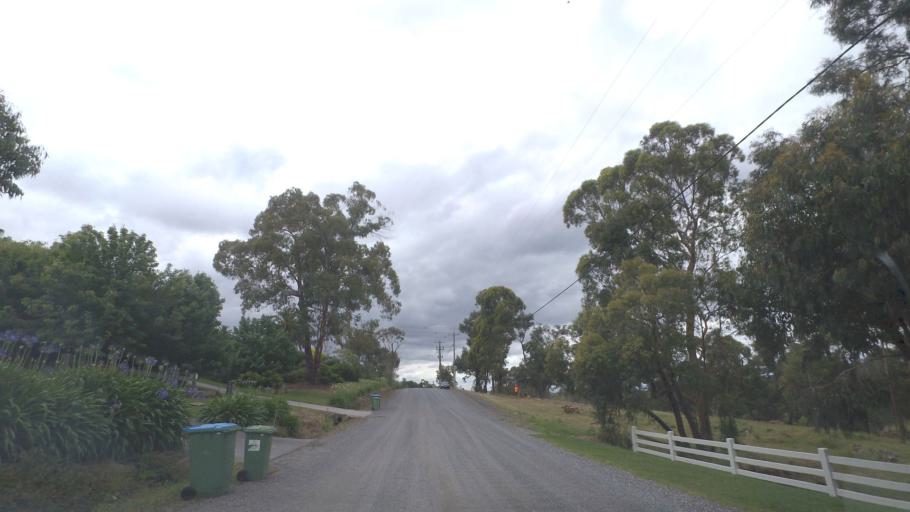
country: AU
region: Victoria
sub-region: Maroondah
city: Warranwood
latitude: -37.7666
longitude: 145.2445
